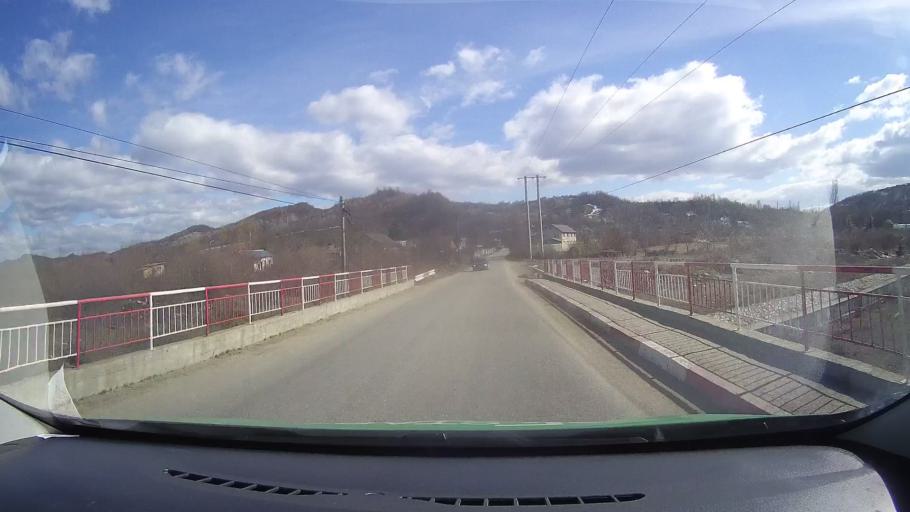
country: RO
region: Dambovita
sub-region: Comuna Branesti
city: Branesti
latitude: 45.0308
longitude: 25.4197
